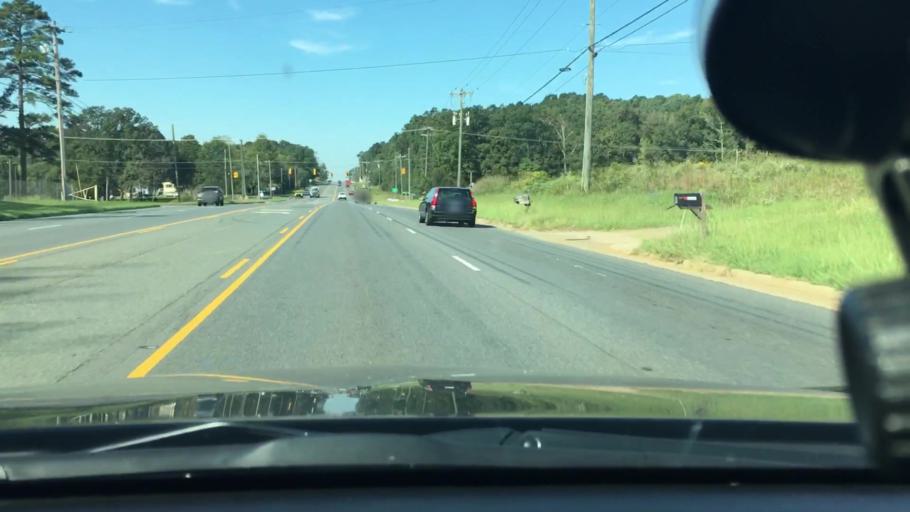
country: US
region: North Carolina
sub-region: Cabarrus County
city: Midland
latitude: 35.2496
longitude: -80.5367
